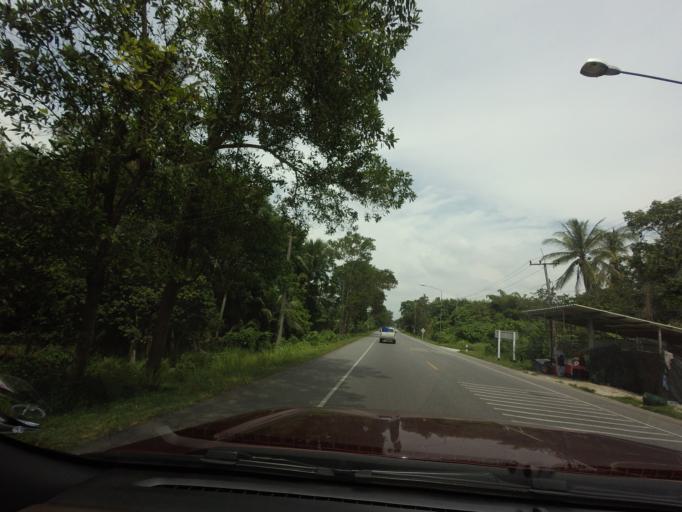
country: TH
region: Yala
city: Yala
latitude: 6.6024
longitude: 101.3026
